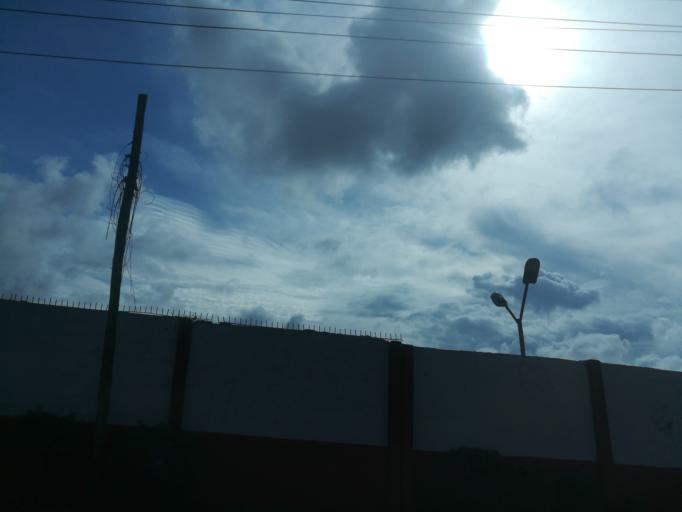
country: NG
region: Lagos
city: Ikeja
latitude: 6.6168
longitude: 3.3533
